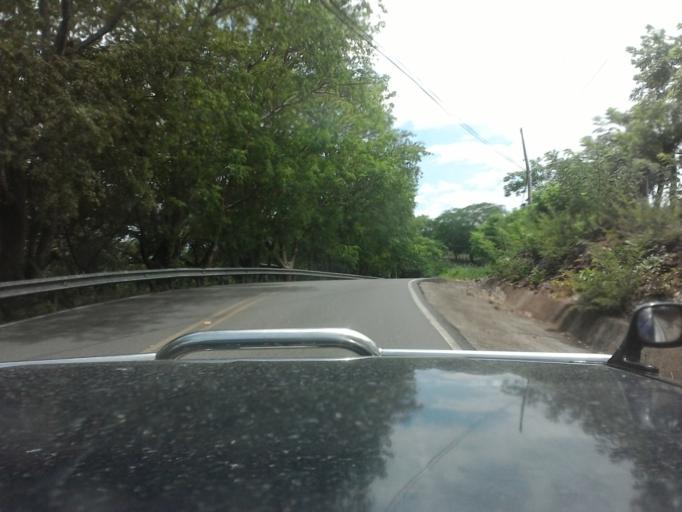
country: CR
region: Puntarenas
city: Miramar
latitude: 10.1444
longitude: -84.8496
